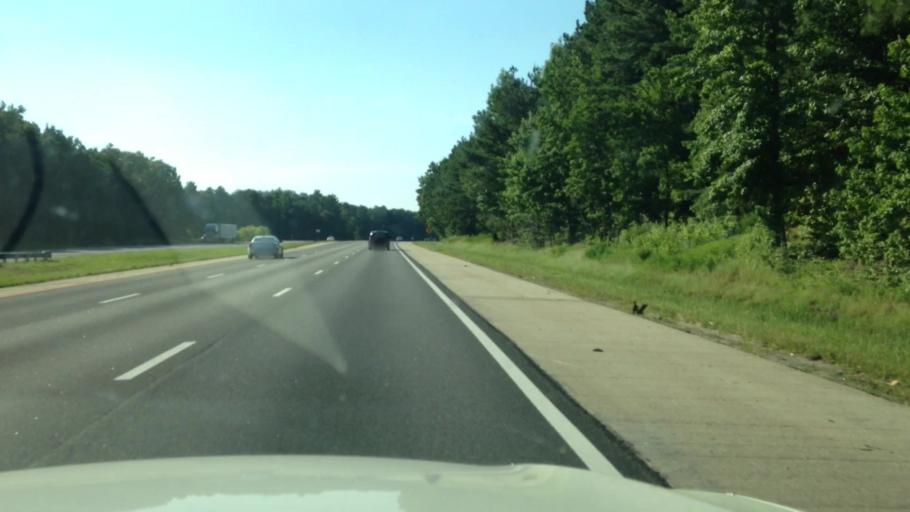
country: US
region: Virginia
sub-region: Chesterfield County
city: Enon
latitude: 37.3608
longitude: -77.3414
